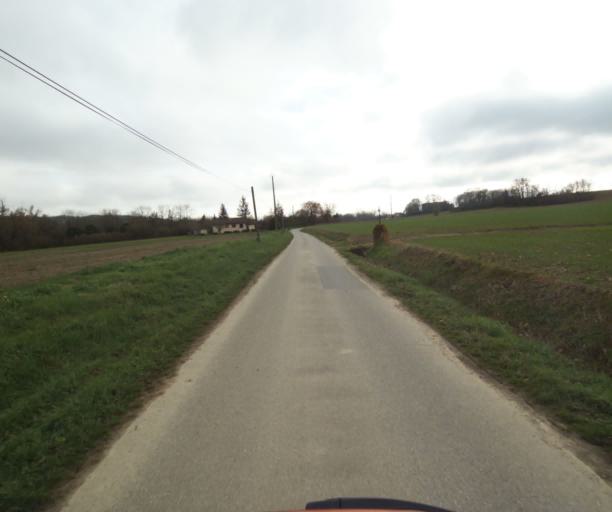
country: FR
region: Languedoc-Roussillon
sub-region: Departement de l'Aude
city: Belpech
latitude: 43.1814
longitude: 1.7343
